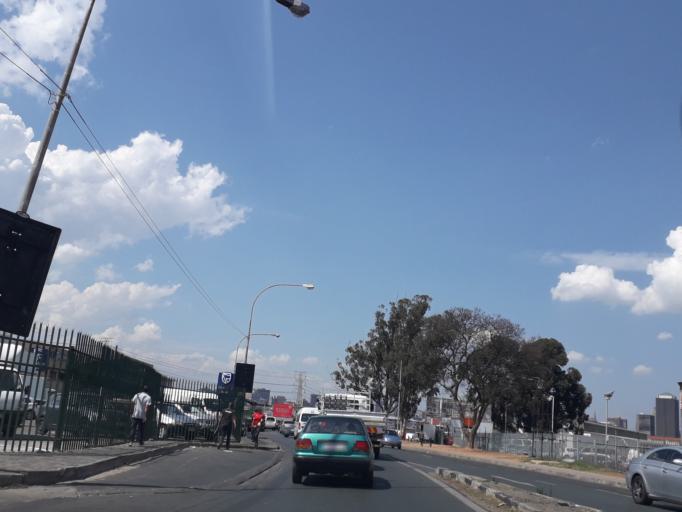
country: ZA
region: Gauteng
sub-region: City of Johannesburg Metropolitan Municipality
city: Johannesburg
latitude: -26.2125
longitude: 28.0171
